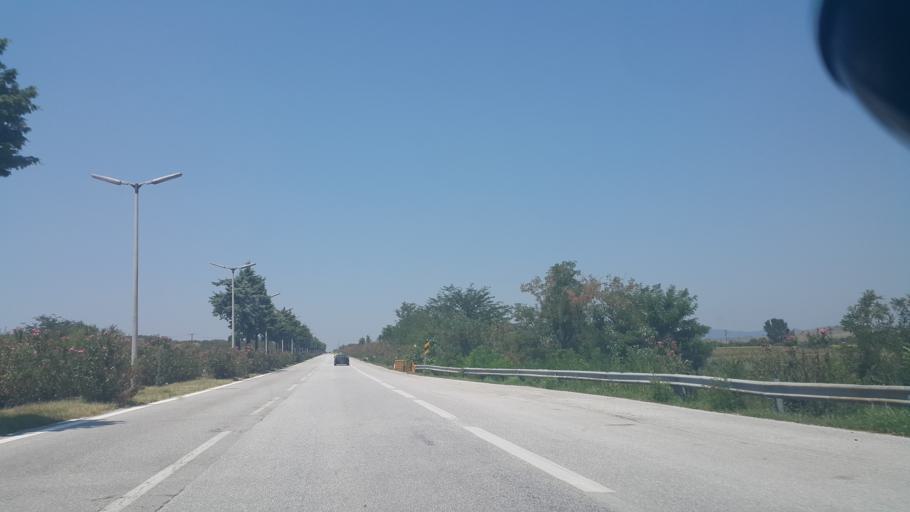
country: MK
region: Bogdanci
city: Stojakovo
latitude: 41.0822
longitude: 22.5877
